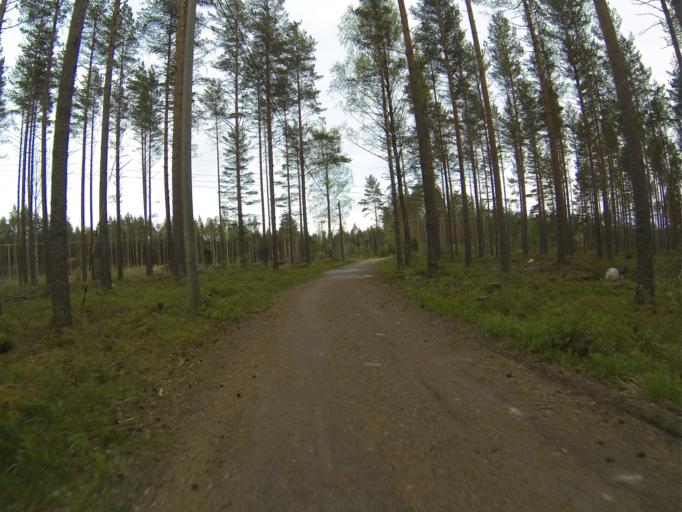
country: FI
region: Varsinais-Suomi
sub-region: Salo
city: Salo
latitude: 60.3858
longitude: 23.1840
